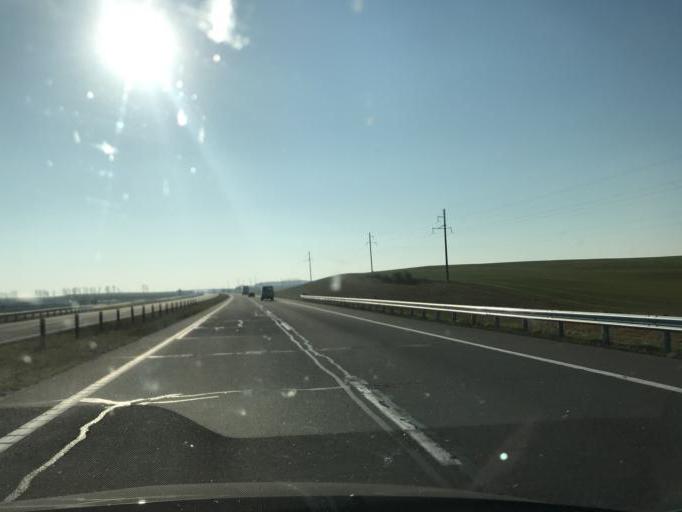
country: BY
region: Minsk
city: Novy Svyerzhan'
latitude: 53.4887
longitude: 26.6371
